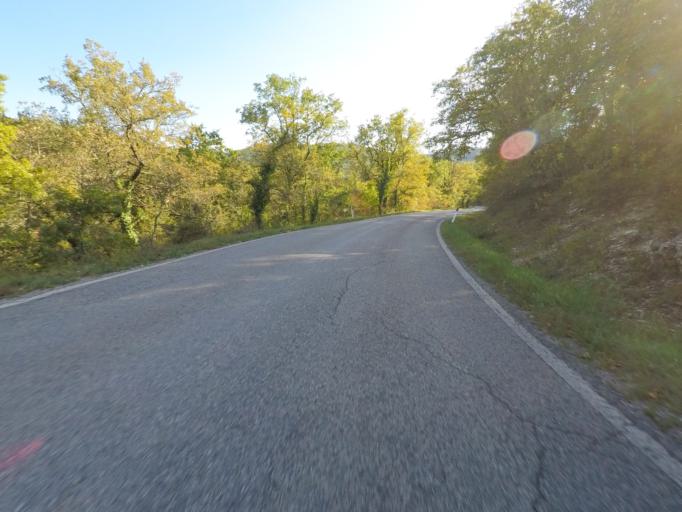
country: IT
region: Tuscany
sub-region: Provincia di Siena
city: Radda in Chianti
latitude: 43.4735
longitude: 11.3744
